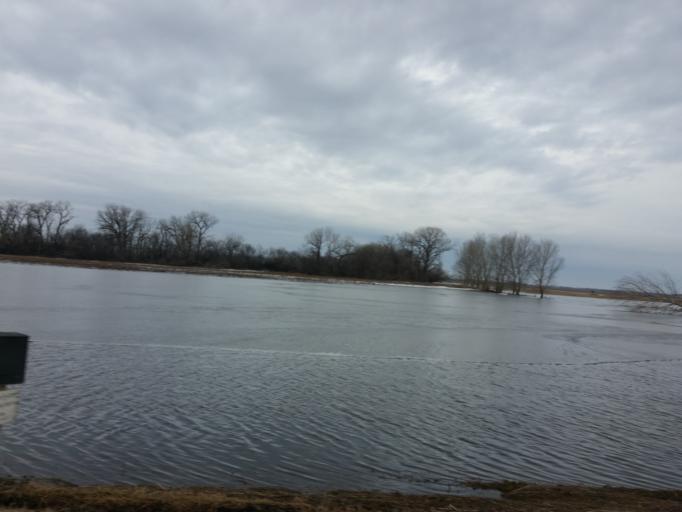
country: US
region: North Dakota
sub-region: Walsh County
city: Grafton
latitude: 48.4049
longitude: -97.4703
